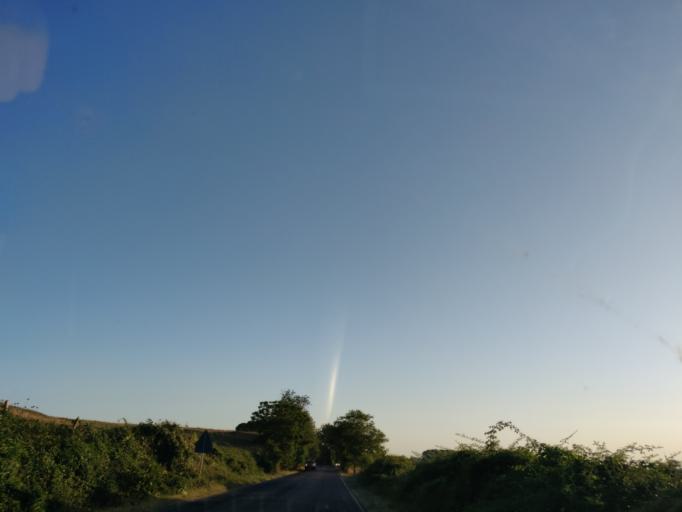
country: IT
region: Latium
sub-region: Provincia di Viterbo
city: Canino
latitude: 42.4109
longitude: 11.6989
